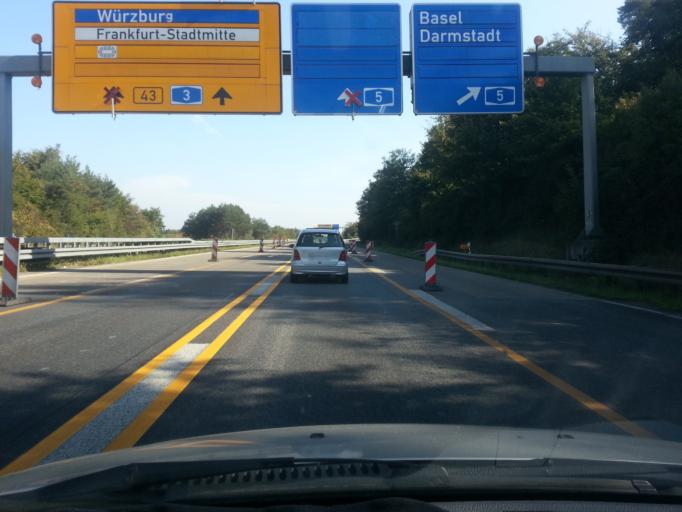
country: DE
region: Hesse
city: Niederrad
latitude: 50.0577
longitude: 8.6010
